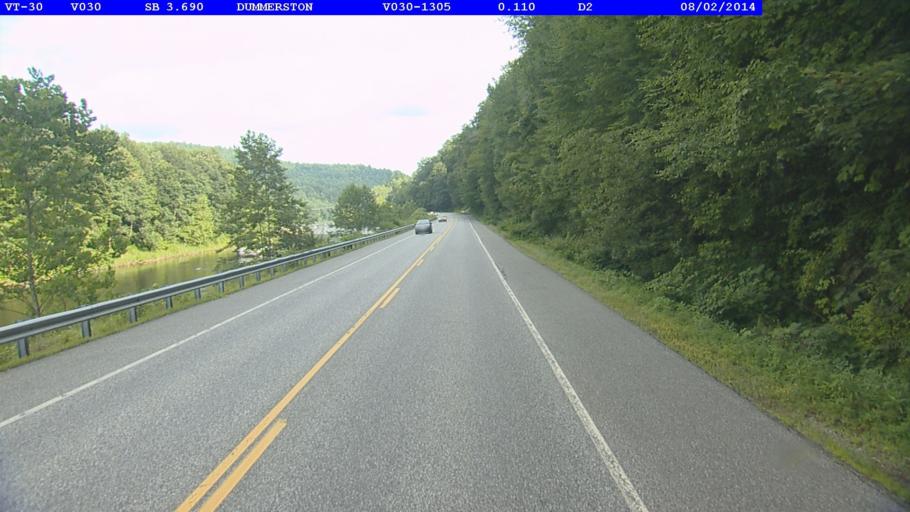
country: US
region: Vermont
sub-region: Windham County
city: West Brattleboro
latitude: 42.8988
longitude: -72.5998
